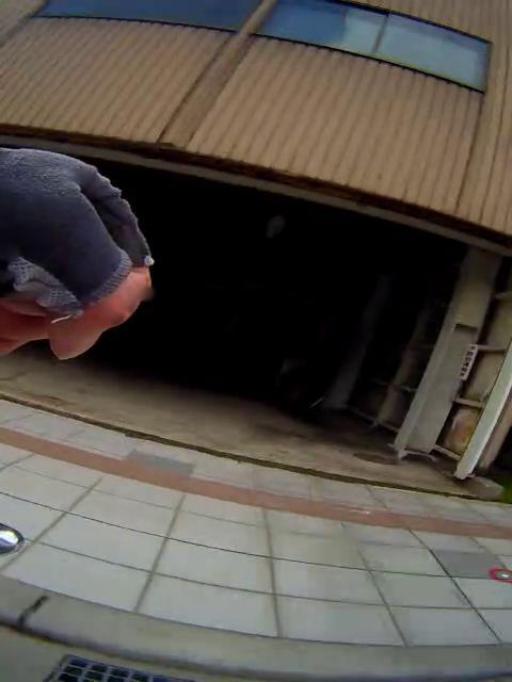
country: JP
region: Toyama
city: Takaoka
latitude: 36.7423
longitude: 137.0066
